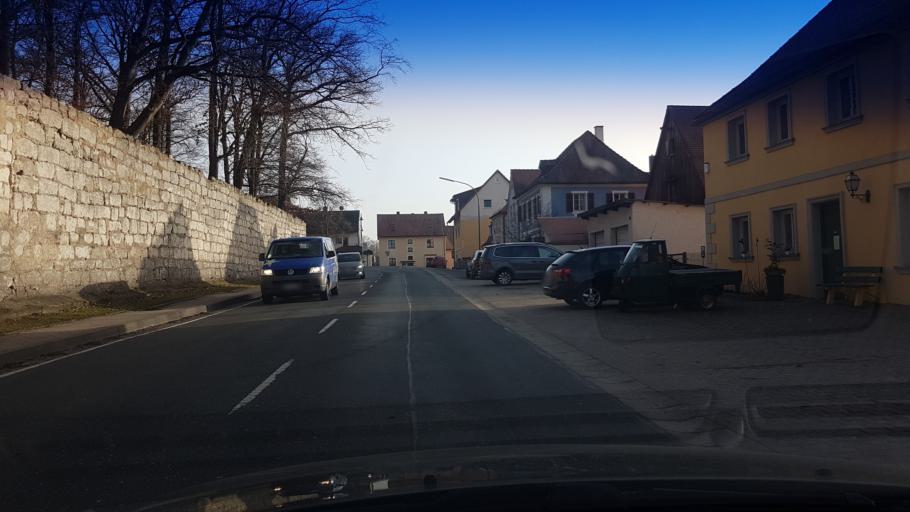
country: DE
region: Bavaria
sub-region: Upper Franconia
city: Pommersfelden
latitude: 49.7632
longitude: 10.8164
